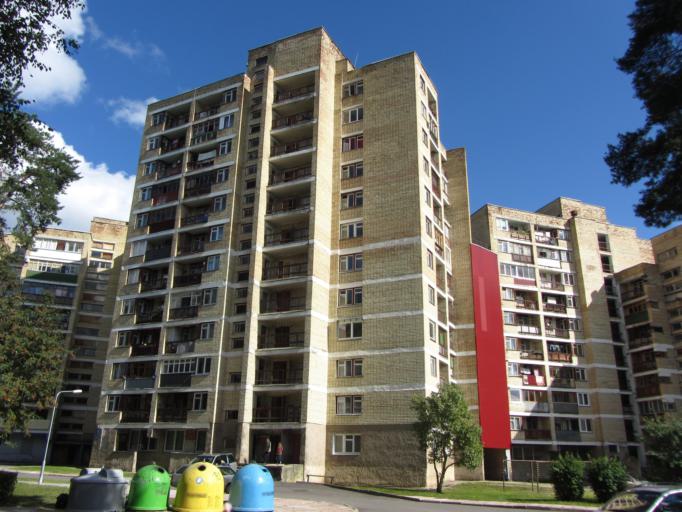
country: LT
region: Utenos apskritis
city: Visaginas
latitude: 55.5974
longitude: 26.4192
